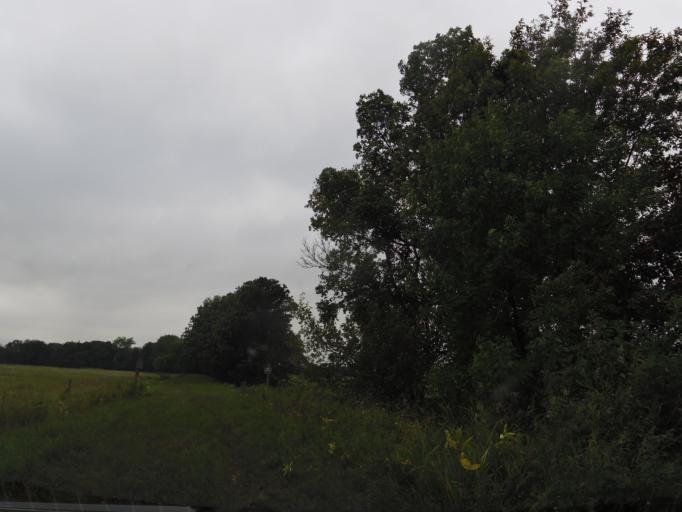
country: US
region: North Dakota
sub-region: Walsh County
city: Grafton
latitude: 48.4277
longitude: -97.1293
